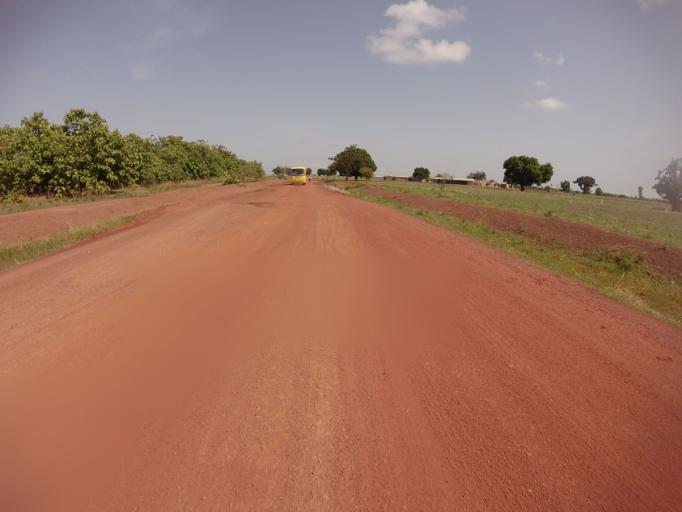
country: GH
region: Upper East
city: Bawku
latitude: 11.0087
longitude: -0.2009
